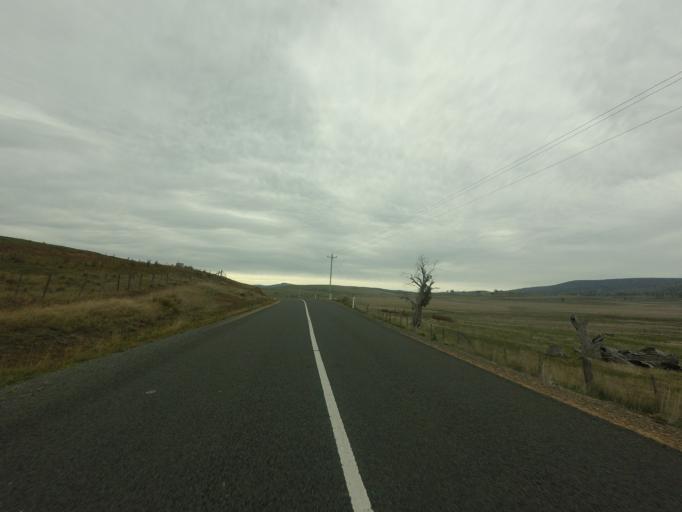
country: AU
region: Tasmania
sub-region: Derwent Valley
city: New Norfolk
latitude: -42.4327
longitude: 146.9855
